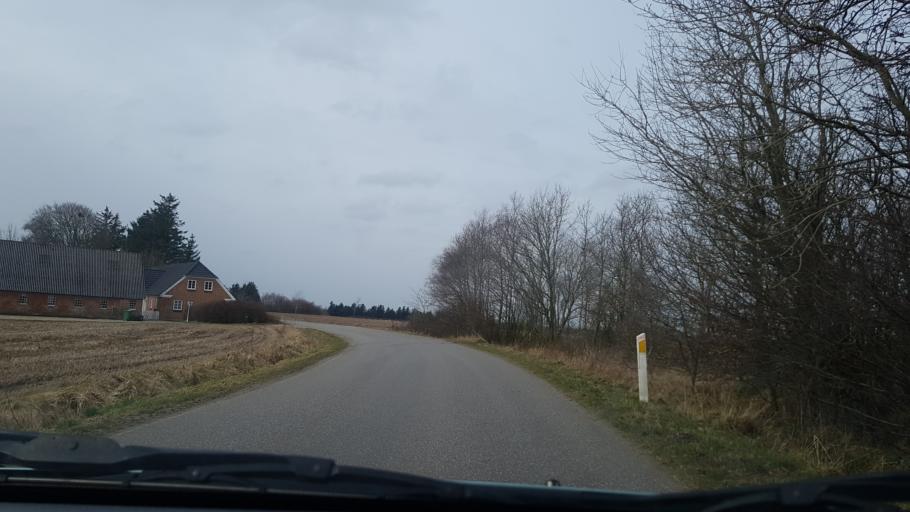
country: DK
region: Central Jutland
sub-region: Holstebro Kommune
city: Ulfborg
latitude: 56.2982
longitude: 8.3563
